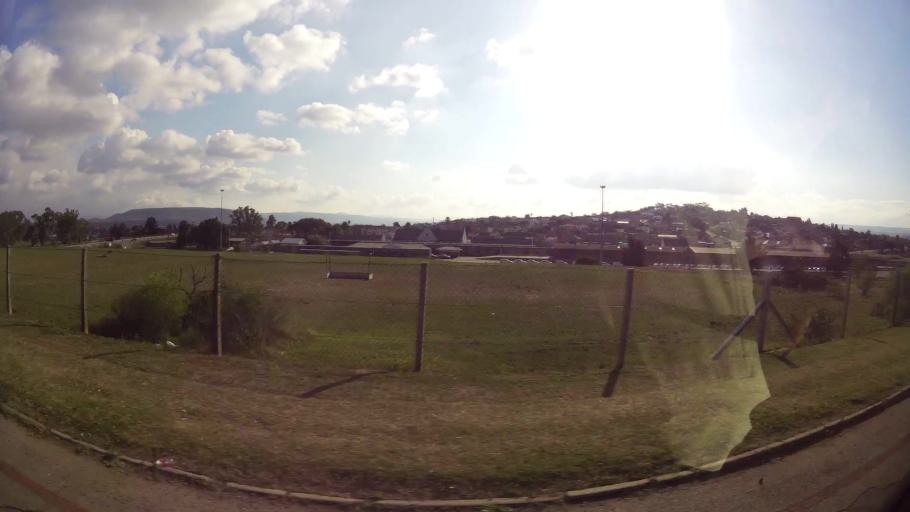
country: ZA
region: Eastern Cape
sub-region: Nelson Mandela Bay Metropolitan Municipality
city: Uitenhage
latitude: -33.7725
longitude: 25.4110
